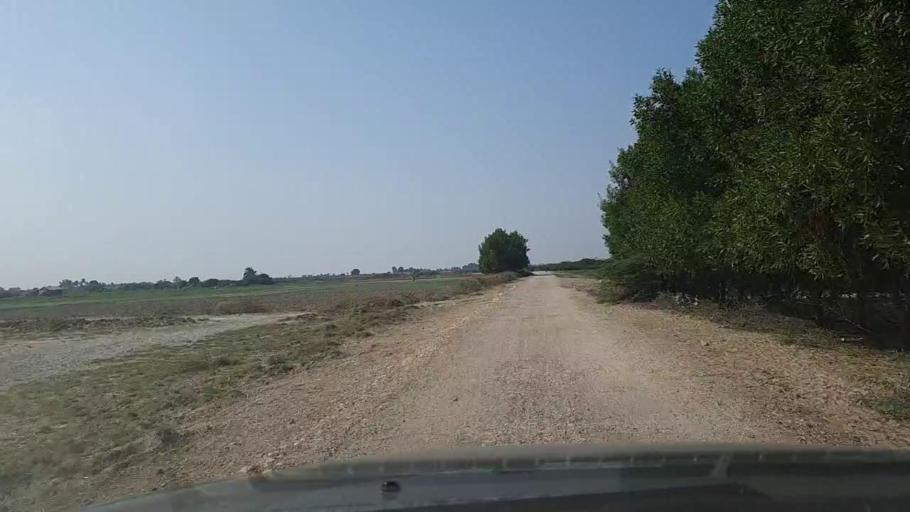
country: PK
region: Sindh
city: Mirpur Sakro
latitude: 24.4060
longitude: 67.6765
